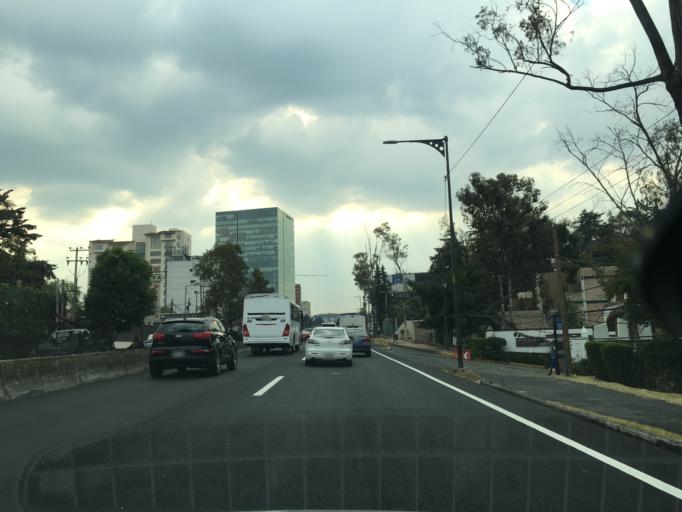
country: MX
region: Mexico City
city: Cuajimalpa
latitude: 19.3646
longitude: -99.2770
